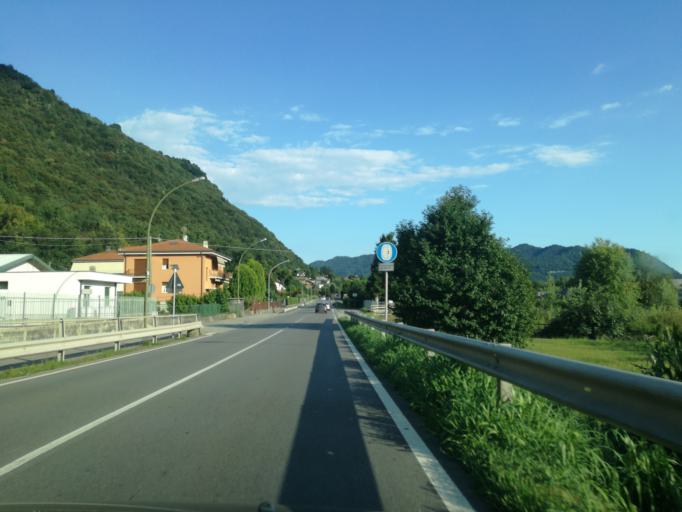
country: IT
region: Lombardy
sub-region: Provincia di Lecco
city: Monte Marenzo
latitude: 45.7613
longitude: 9.4498
